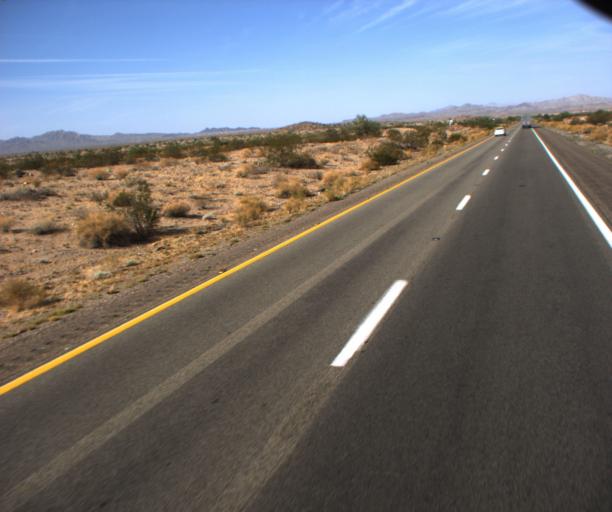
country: US
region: Arizona
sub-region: Mohave County
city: Desert Hills
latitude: 34.7508
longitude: -114.2241
